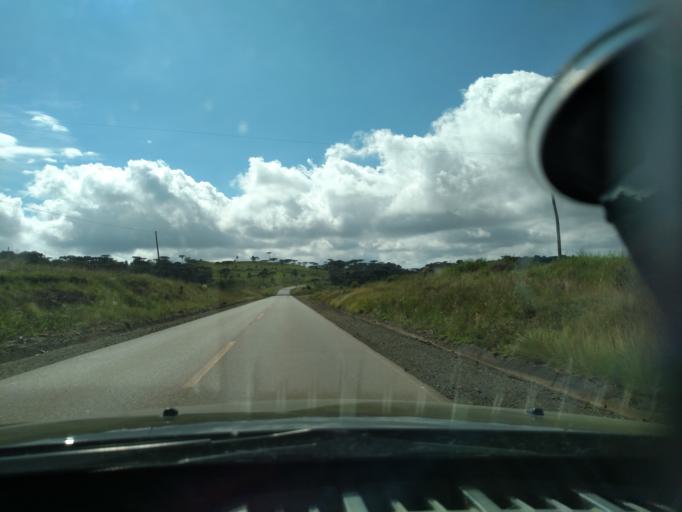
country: BR
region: Santa Catarina
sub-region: Lages
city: Lages
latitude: -27.8938
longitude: -50.1356
